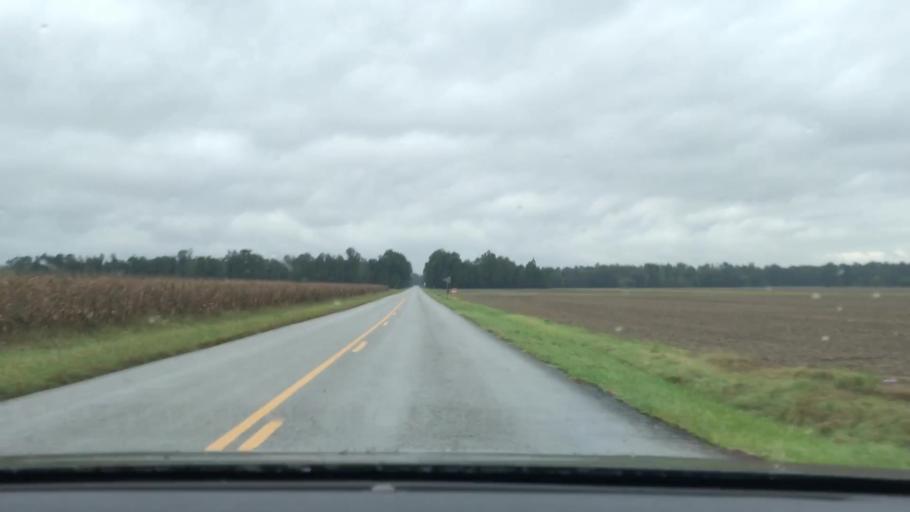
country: US
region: Kentucky
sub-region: McLean County
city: Calhoun
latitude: 37.3974
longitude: -87.2844
